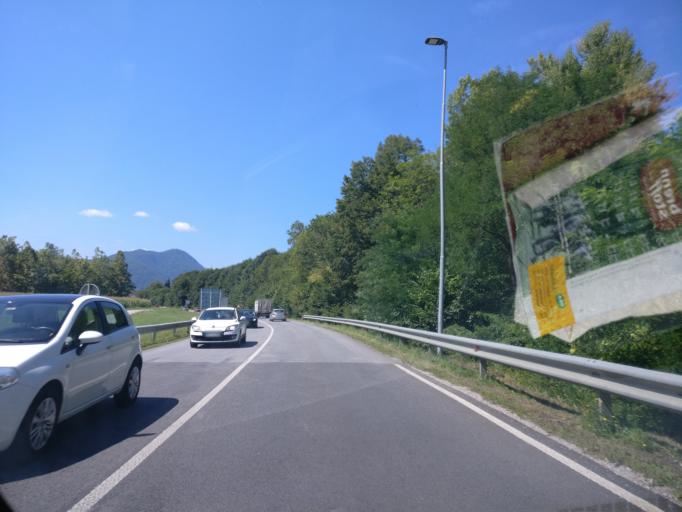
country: SI
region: Skofja Loka
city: Sv. Duh
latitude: 46.1693
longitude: 14.3448
